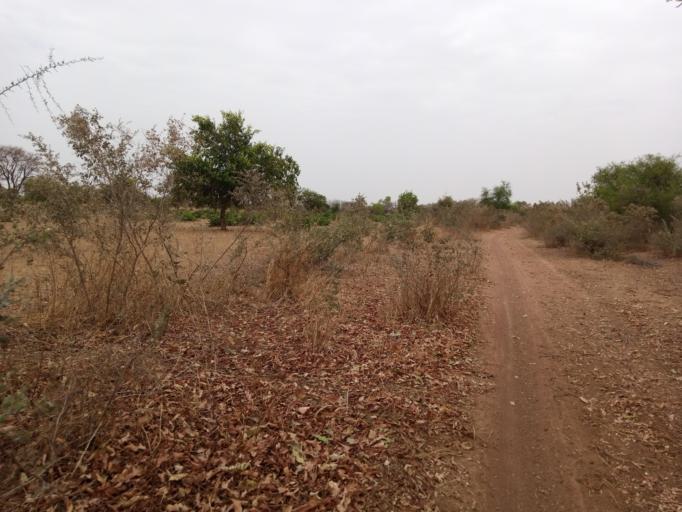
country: BF
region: Boucle du Mouhoun
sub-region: Province de la Kossi
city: Nouna
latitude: 12.8403
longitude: -4.0769
